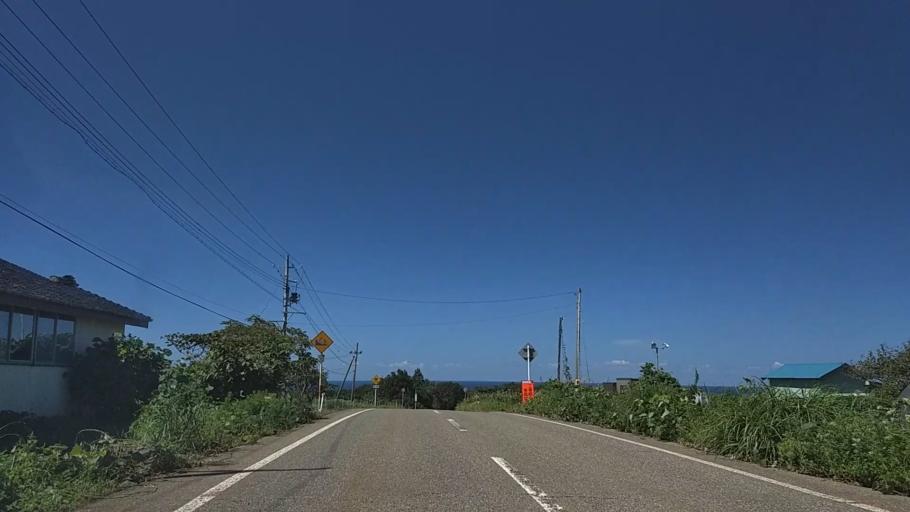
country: JP
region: Niigata
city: Joetsu
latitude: 37.1702
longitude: 138.1065
